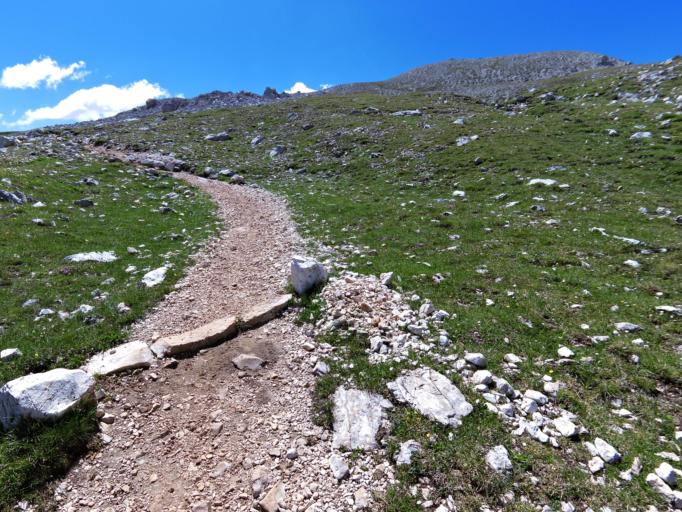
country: IT
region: Trentino-Alto Adige
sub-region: Bolzano
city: Siusi
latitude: 46.5040
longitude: 11.5955
